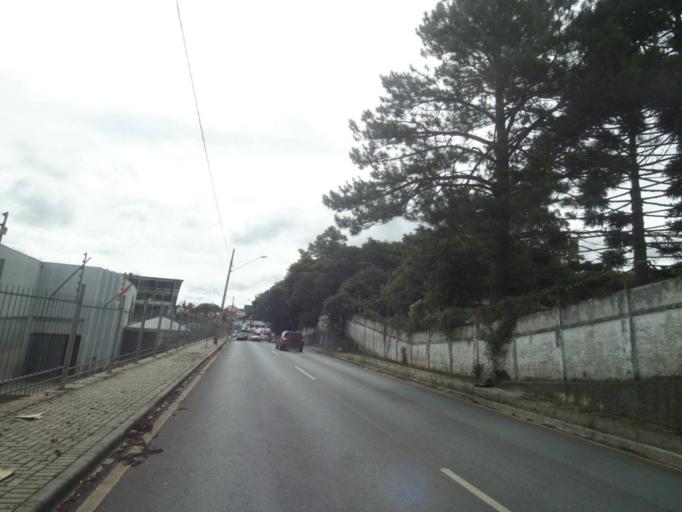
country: BR
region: Parana
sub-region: Curitiba
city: Curitiba
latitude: -25.4423
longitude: -49.3040
